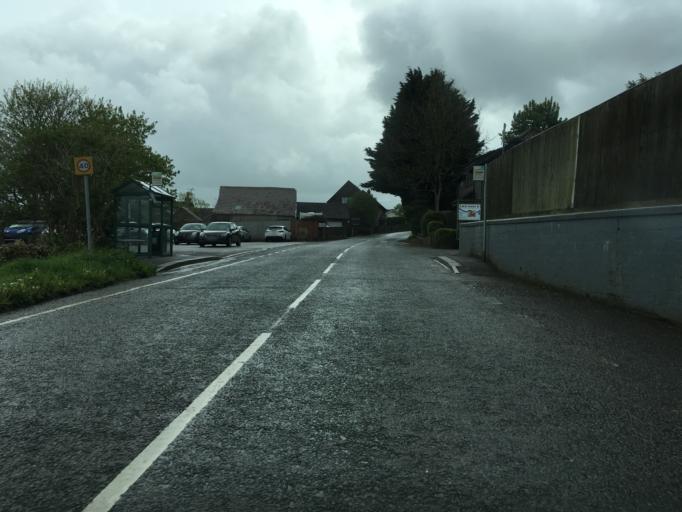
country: GB
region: England
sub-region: Bath and North East Somerset
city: Compton Martin
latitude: 51.3181
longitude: -2.6783
